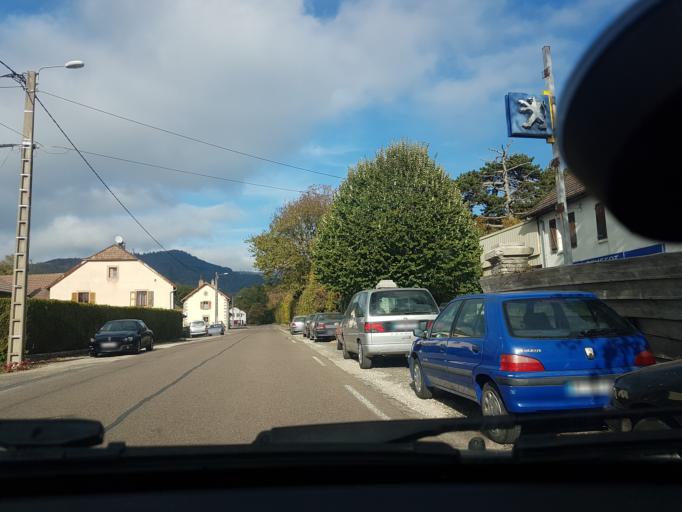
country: FR
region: Franche-Comte
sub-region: Departement de la Haute-Saone
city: Plancher-Bas
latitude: 47.7413
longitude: 6.7284
